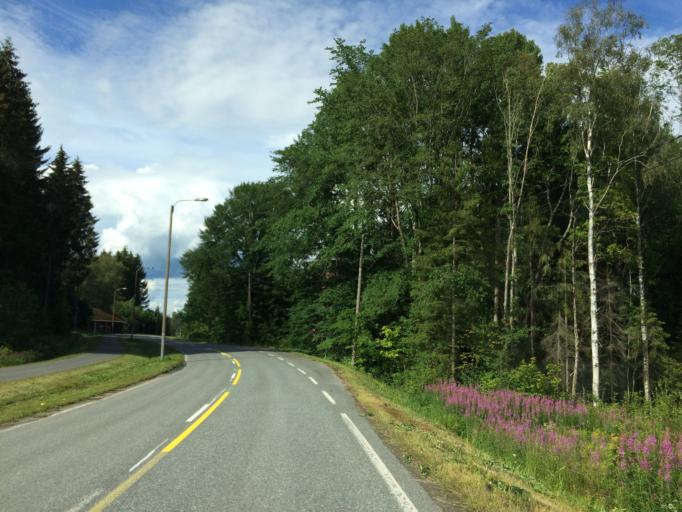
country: FI
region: Haeme
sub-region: Haemeenlinna
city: Janakkala
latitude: 60.9162
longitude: 24.6125
